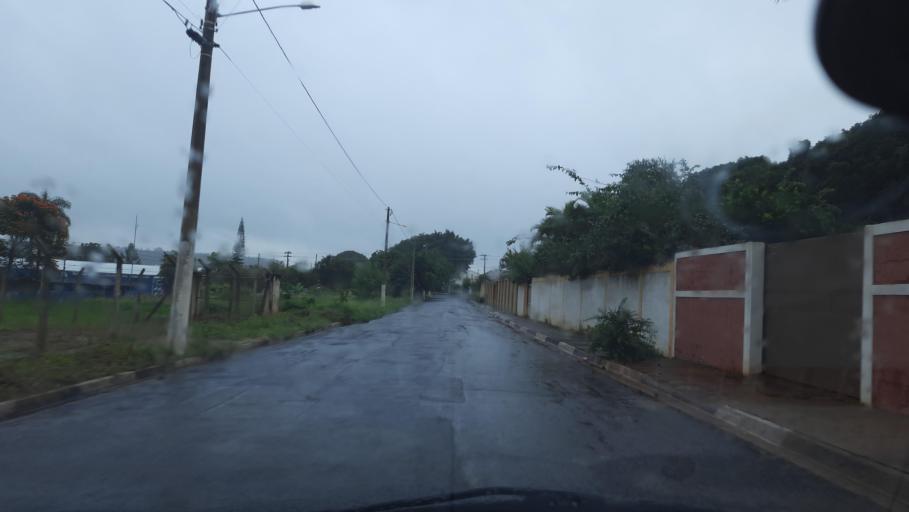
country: BR
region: Sao Paulo
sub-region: Casa Branca
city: Casa Branca
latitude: -21.7811
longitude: -47.0722
